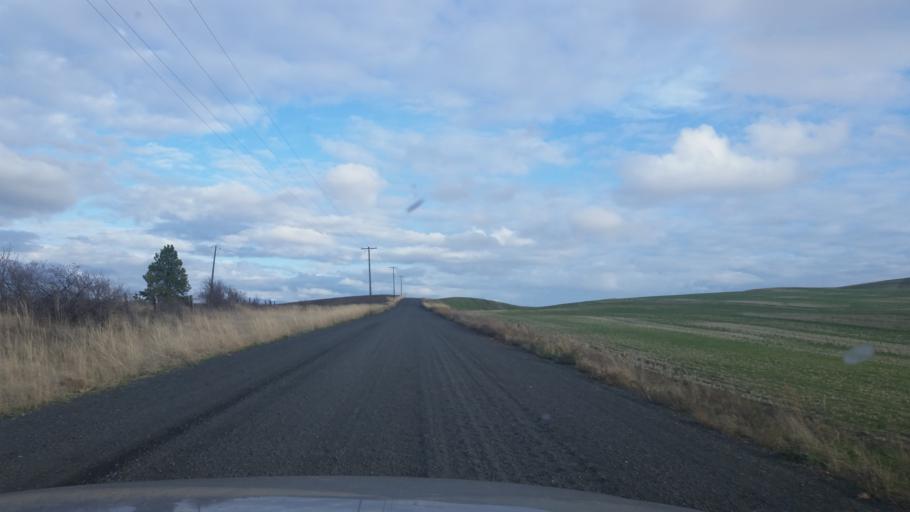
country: US
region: Washington
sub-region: Spokane County
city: Cheney
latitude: 47.4272
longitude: -117.4115
